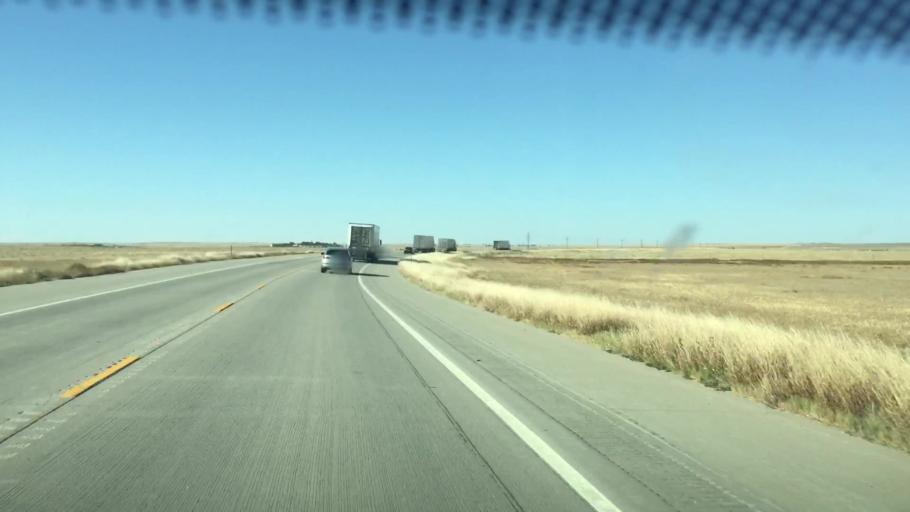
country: US
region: Colorado
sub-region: Kiowa County
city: Eads
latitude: 38.3729
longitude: -102.7288
